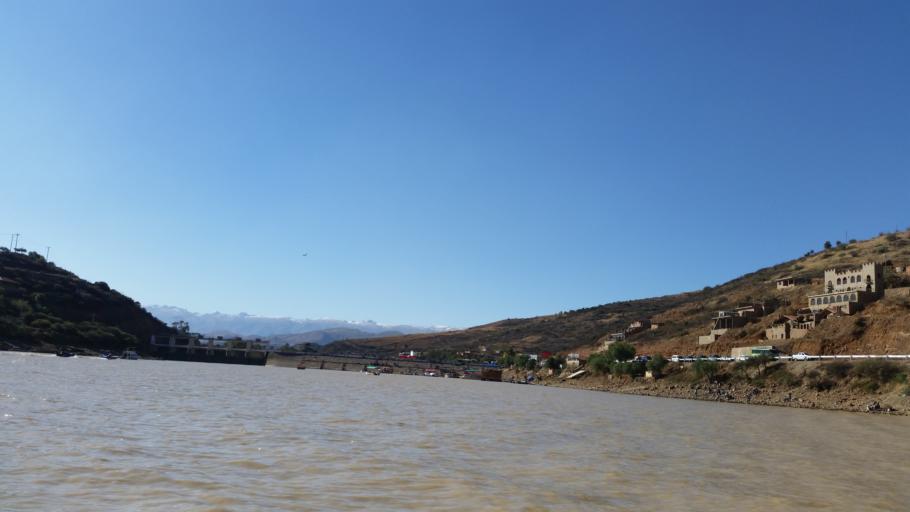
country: BO
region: Cochabamba
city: Tarata
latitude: -17.5319
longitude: -66.0858
